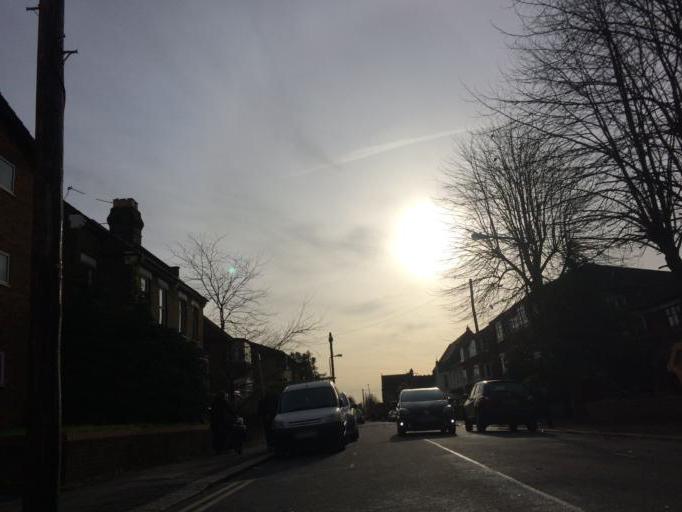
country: GB
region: England
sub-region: Greater London
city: Walthamstow
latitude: 51.5827
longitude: -0.0155
